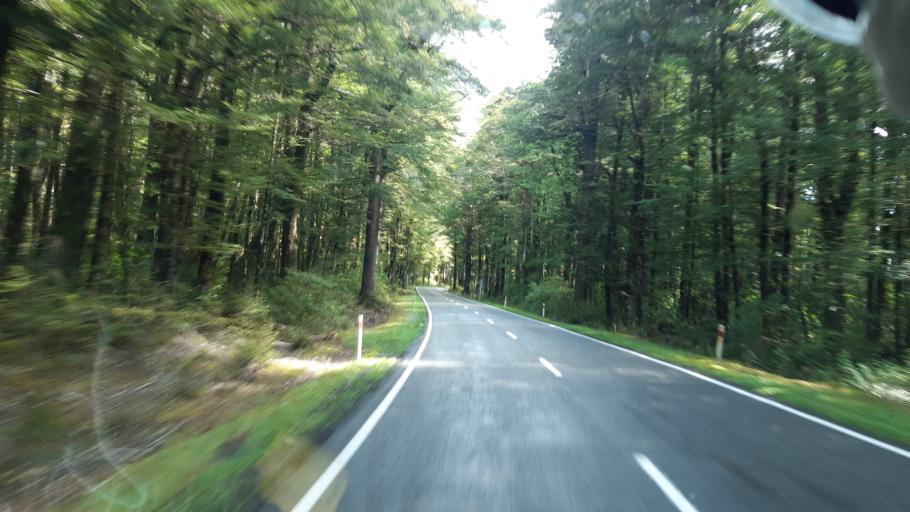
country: NZ
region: Canterbury
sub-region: Hurunui District
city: Amberley
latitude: -42.3807
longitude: 172.3036
